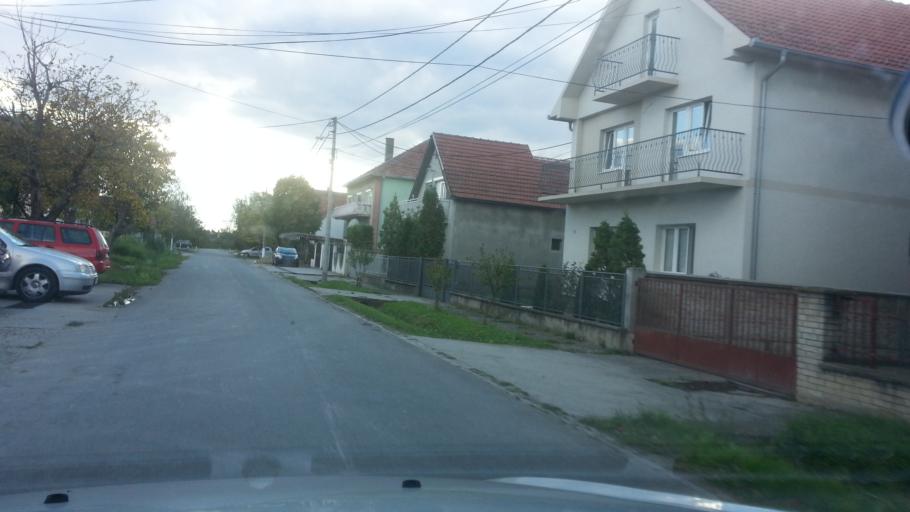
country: RS
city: Novi Banovci
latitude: 44.9042
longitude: 20.2676
